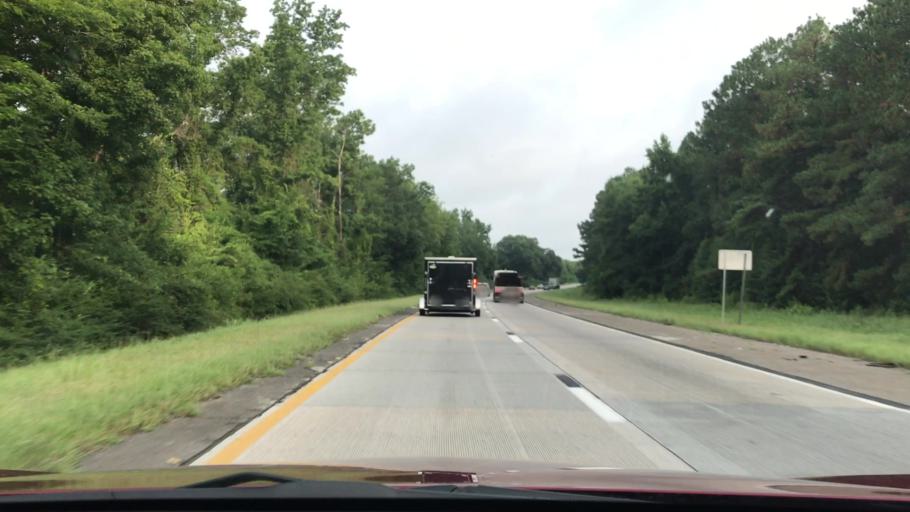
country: US
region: South Carolina
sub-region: Orangeburg County
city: Holly Hill
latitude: 33.2370
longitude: -80.4566
